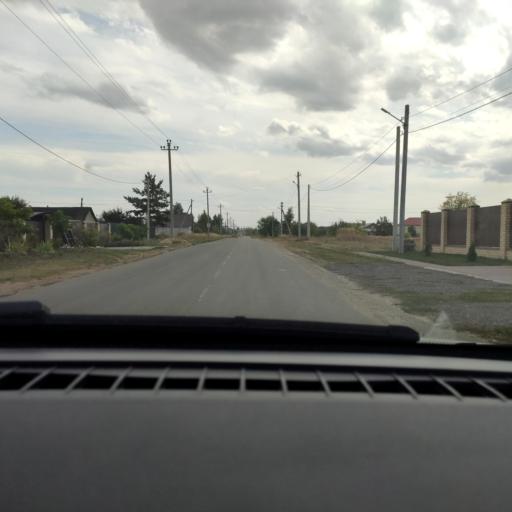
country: RU
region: Voronezj
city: Novaya Usman'
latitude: 51.6676
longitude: 39.4406
